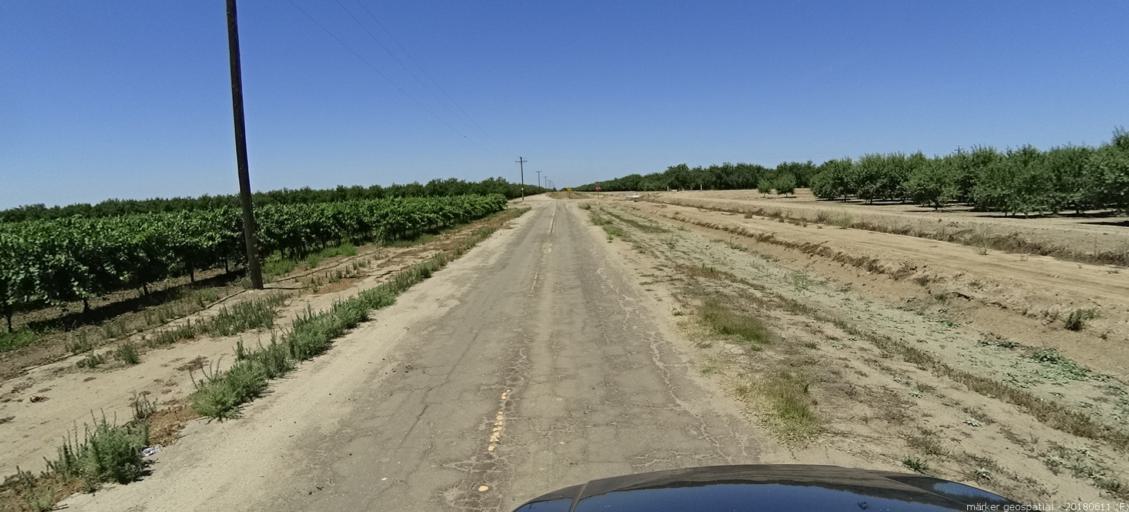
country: US
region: California
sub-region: Madera County
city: Fairmead
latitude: 37.0256
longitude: -120.2193
